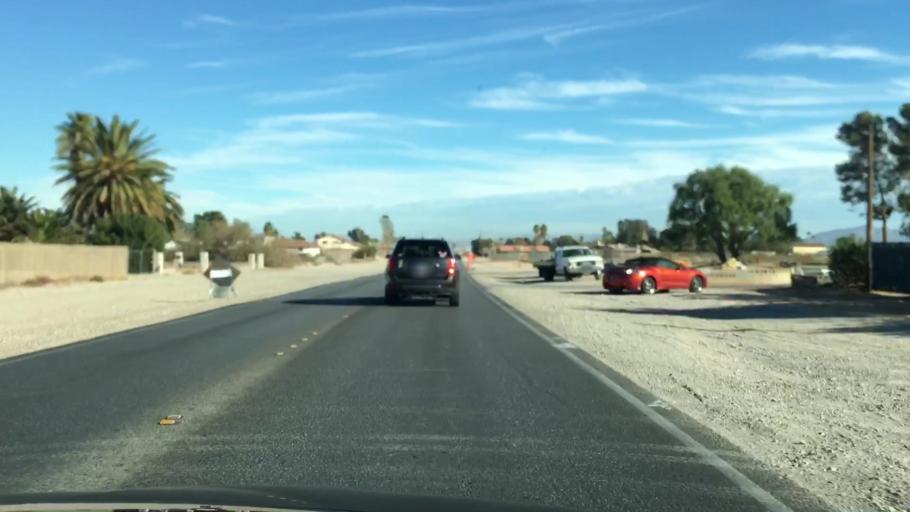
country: US
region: Nevada
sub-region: Clark County
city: Enterprise
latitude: 36.0572
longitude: -115.1968
